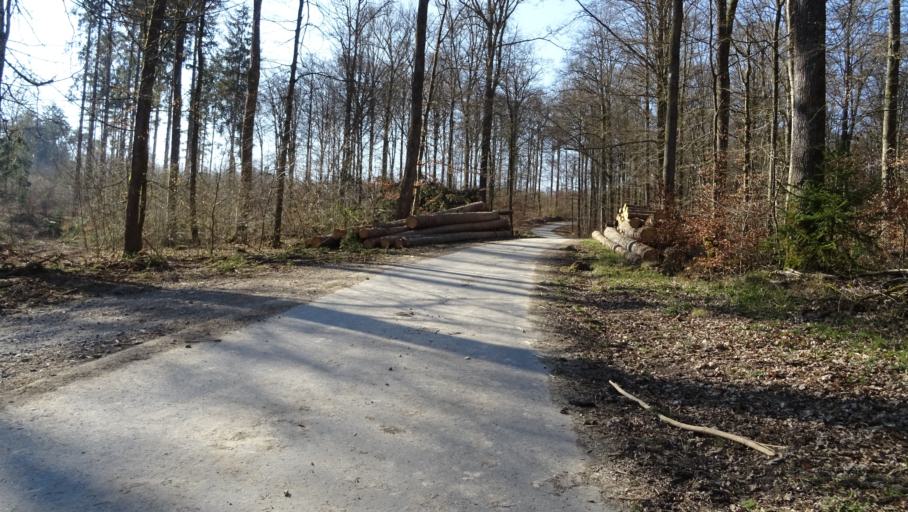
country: DE
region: Baden-Wuerttemberg
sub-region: Regierungsbezirk Stuttgart
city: Roigheim
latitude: 49.3909
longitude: 9.3228
